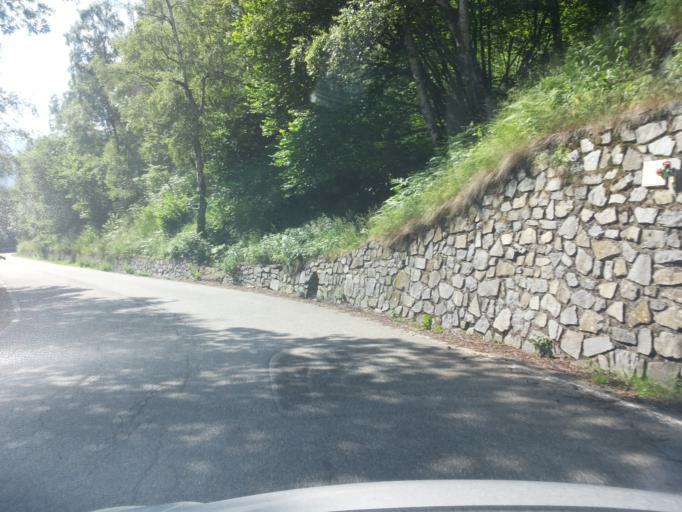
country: IT
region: Piedmont
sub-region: Provincia di Biella
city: Quittengo
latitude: 45.6565
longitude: 8.0361
